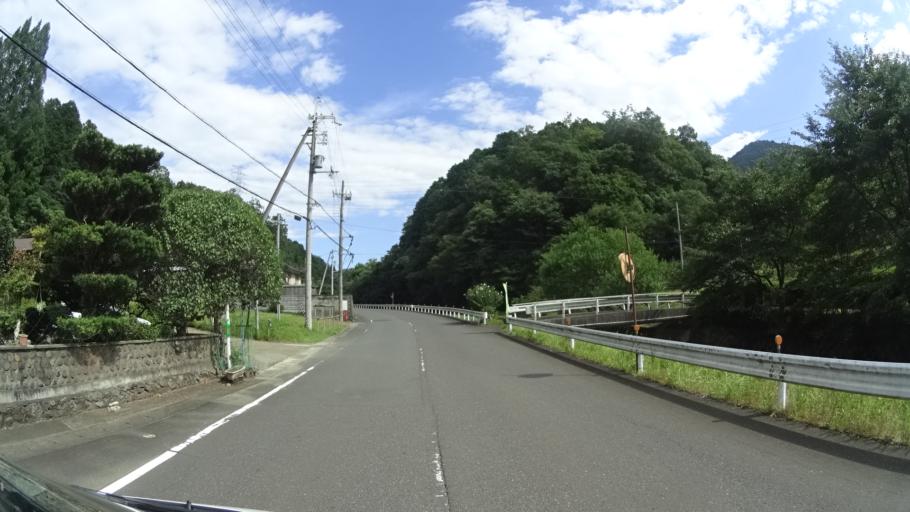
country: JP
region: Kyoto
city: Fukuchiyama
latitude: 35.3612
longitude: 135.1360
